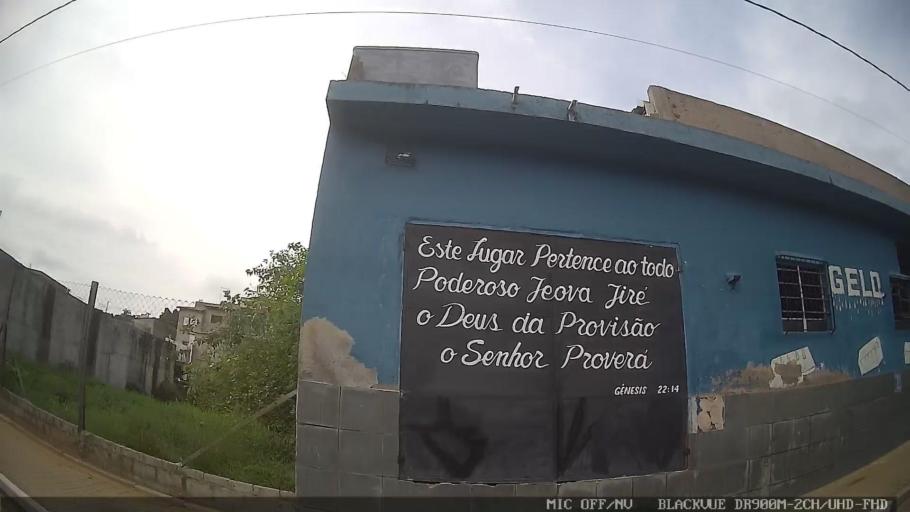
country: BR
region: Sao Paulo
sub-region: Poa
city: Poa
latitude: -23.5183
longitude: -46.3511
